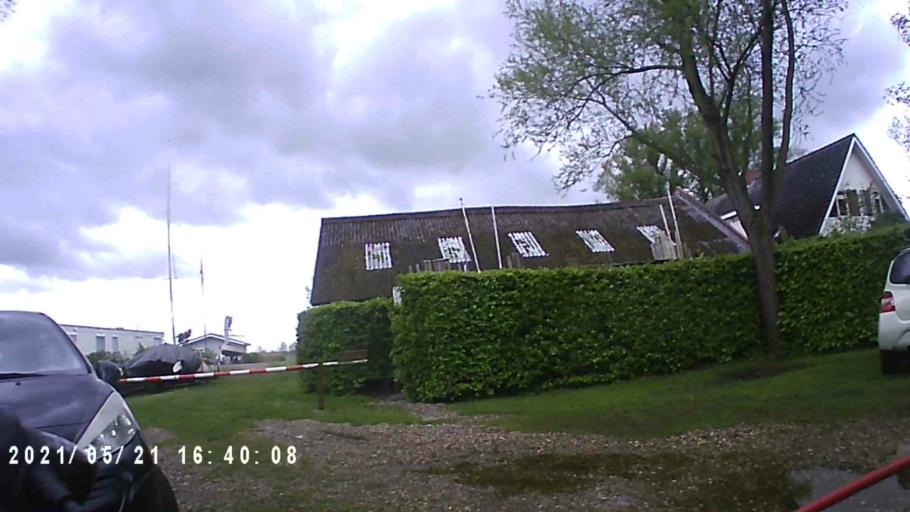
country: NL
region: Groningen
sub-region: Gemeente Zuidhorn
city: Aduard
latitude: 53.1929
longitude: 6.4516
